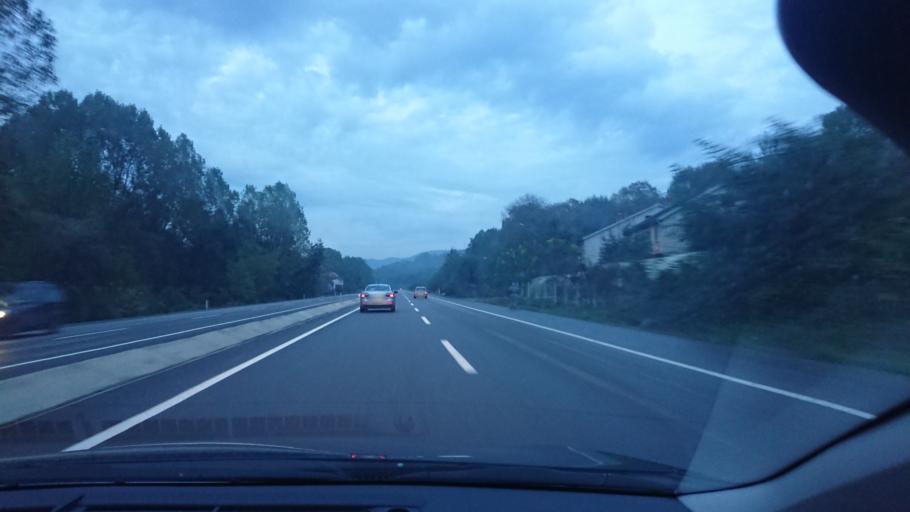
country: TR
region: Zonguldak
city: Gokcebey
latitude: 41.3248
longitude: 32.0563
